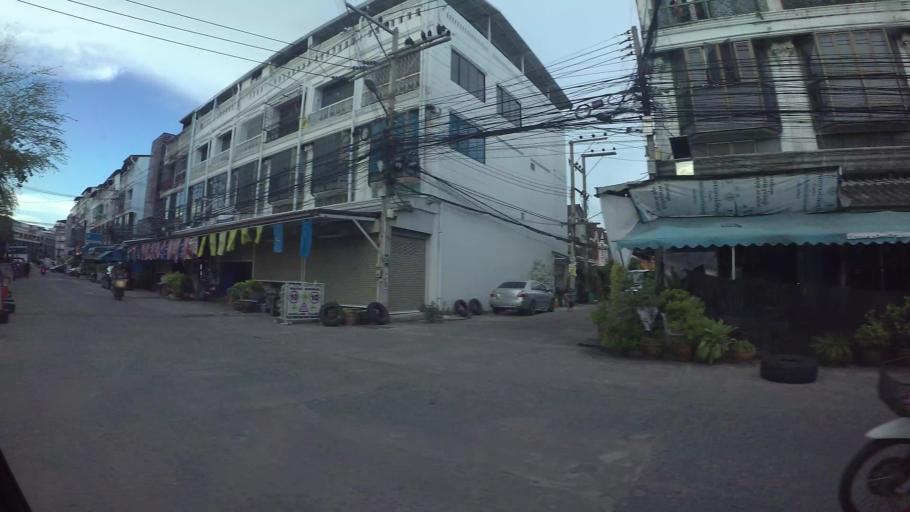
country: TH
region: Chon Buri
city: Phatthaya
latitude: 12.9205
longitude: 100.8826
